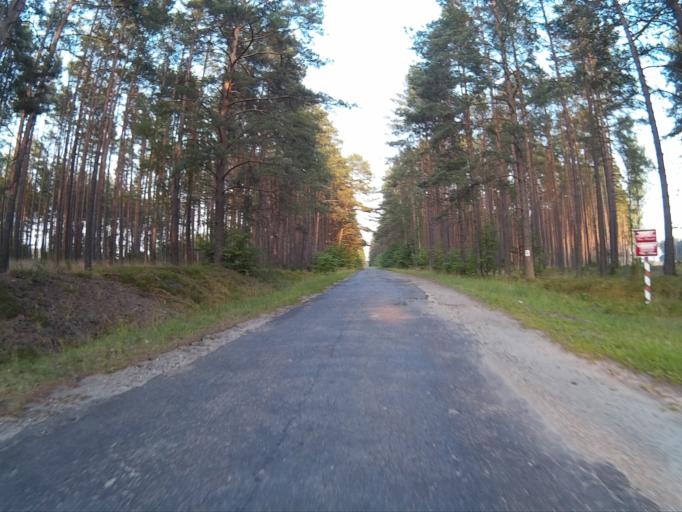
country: PL
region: Kujawsko-Pomorskie
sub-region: Powiat tucholski
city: Tuchola
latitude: 53.7062
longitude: 17.8790
